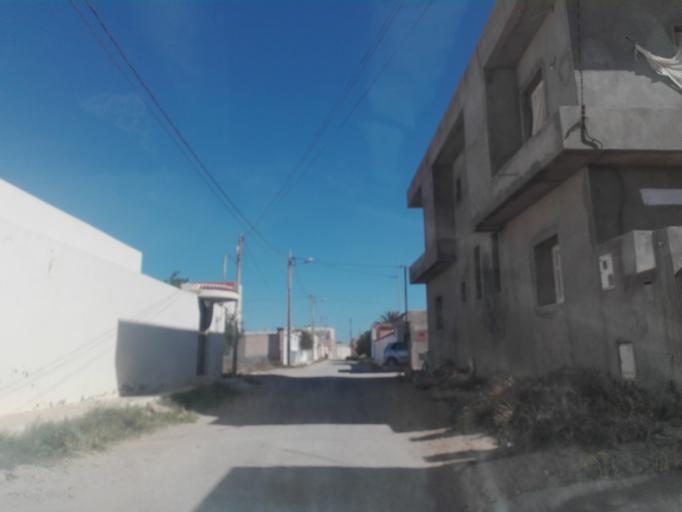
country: TN
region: Safaqis
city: Al Qarmadah
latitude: 34.7111
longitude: 11.2025
